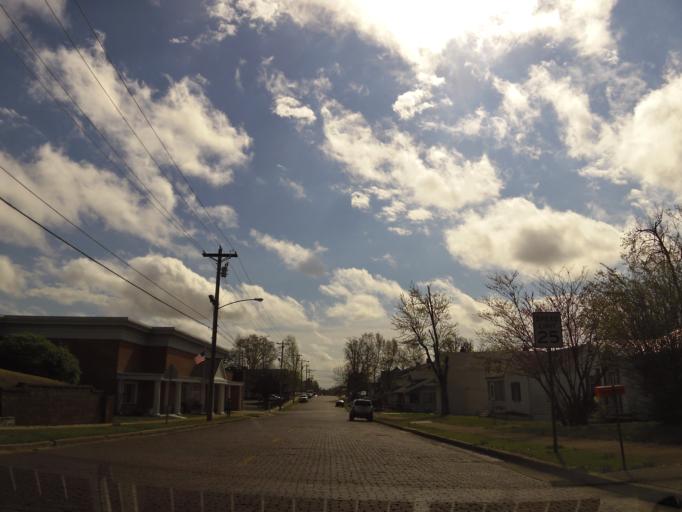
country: US
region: Missouri
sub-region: Butler County
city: Poplar Bluff
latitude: 36.7574
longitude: -90.3998
